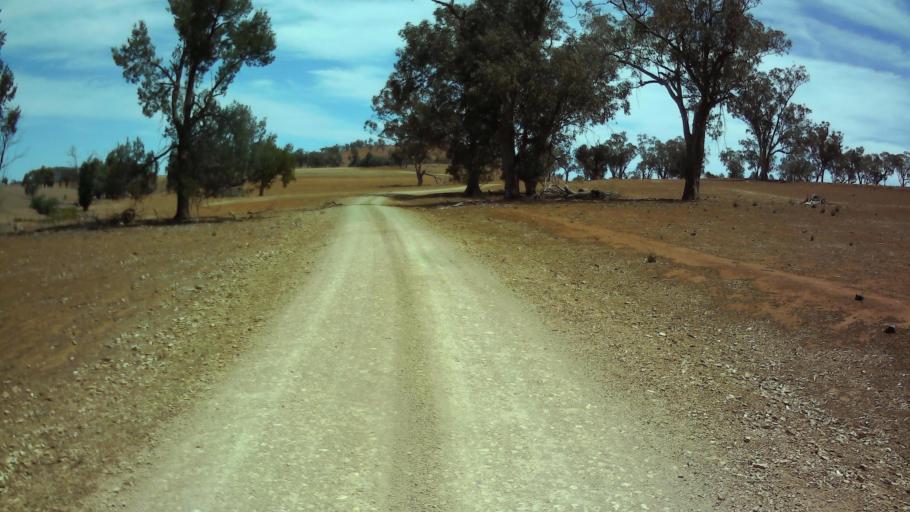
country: AU
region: New South Wales
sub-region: Weddin
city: Grenfell
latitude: -33.7448
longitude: 148.1721
